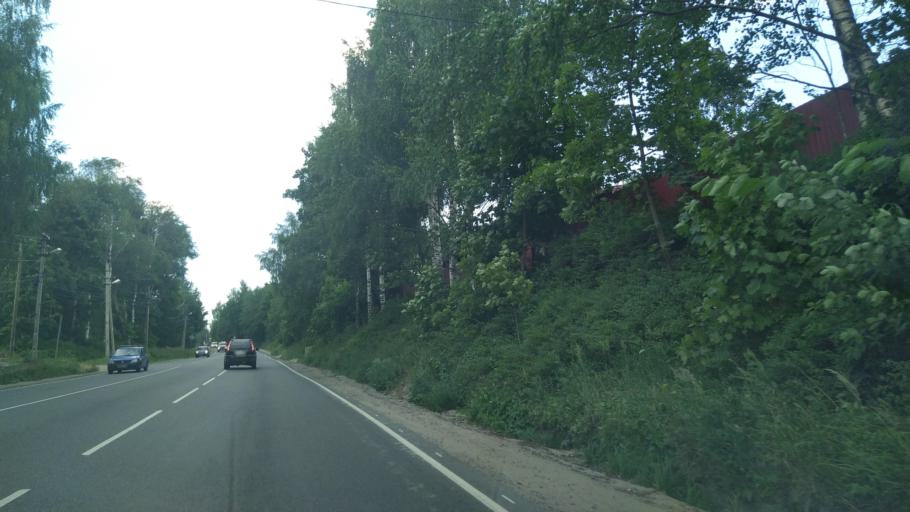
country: RU
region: Leningrad
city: Toksovo
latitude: 60.1578
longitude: 30.5332
